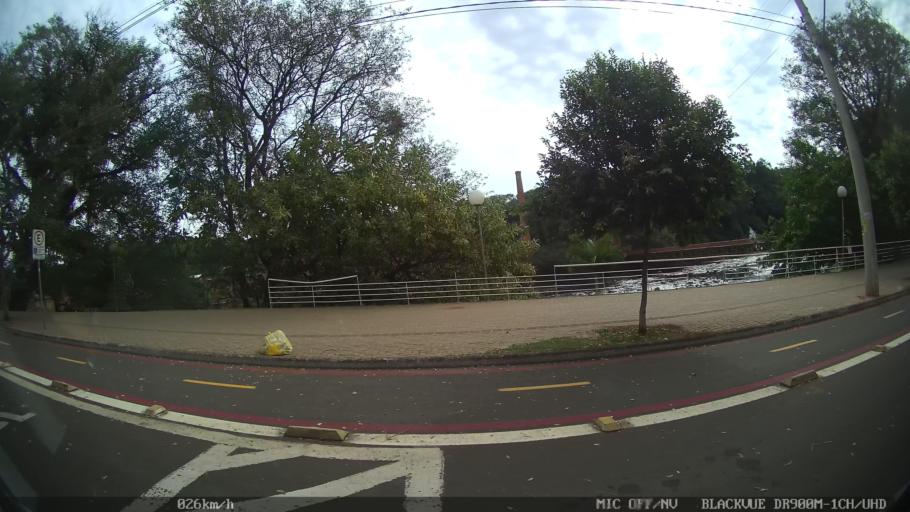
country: BR
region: Sao Paulo
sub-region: Piracicaba
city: Piracicaba
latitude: -22.7186
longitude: -47.6540
